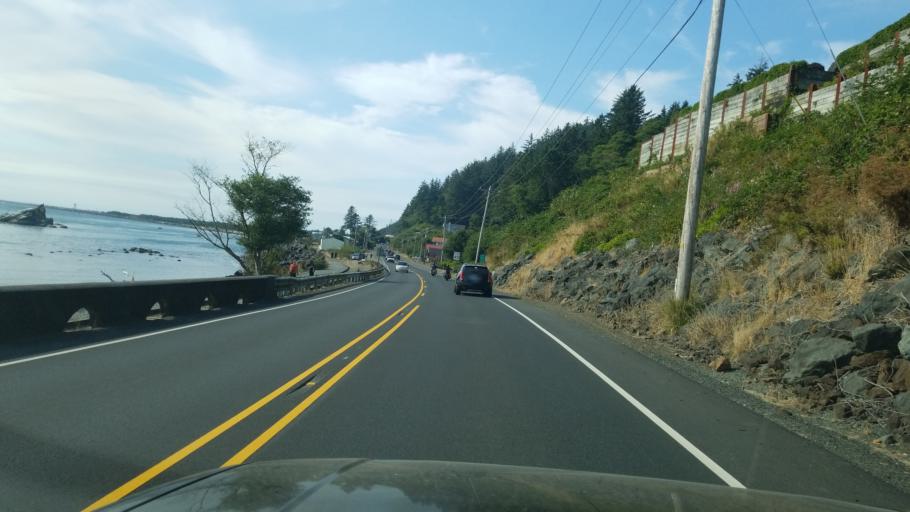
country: US
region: Oregon
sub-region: Tillamook County
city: Rockaway Beach
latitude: 45.5630
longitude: -123.9350
